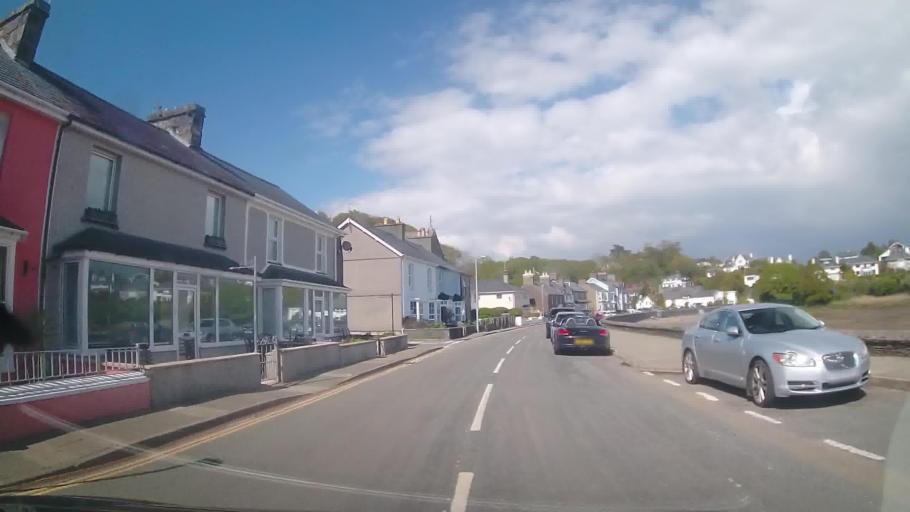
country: GB
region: Wales
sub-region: Gwynedd
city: Porthmadog
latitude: 52.9164
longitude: -4.1366
